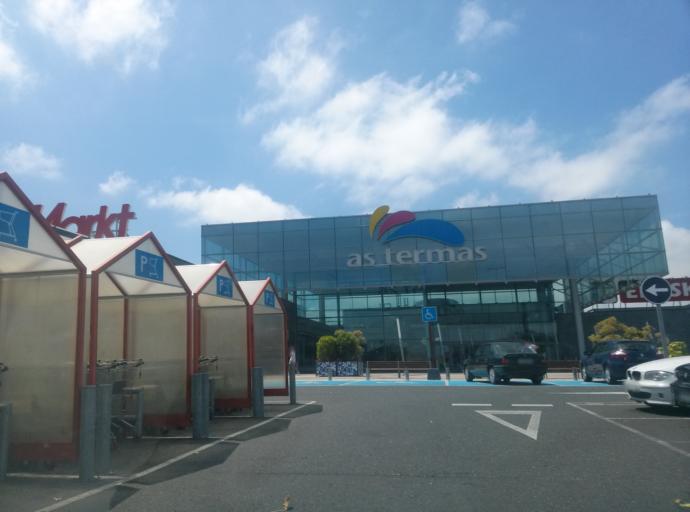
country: ES
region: Galicia
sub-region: Provincia de Lugo
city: Lugo
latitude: 43.0379
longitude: -7.5684
